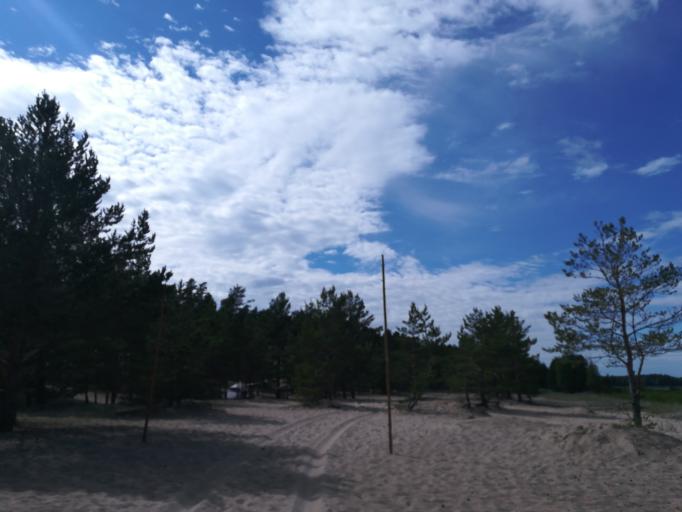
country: RU
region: Leningrad
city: Ust'-Luga
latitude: 59.6808
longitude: 28.2328
